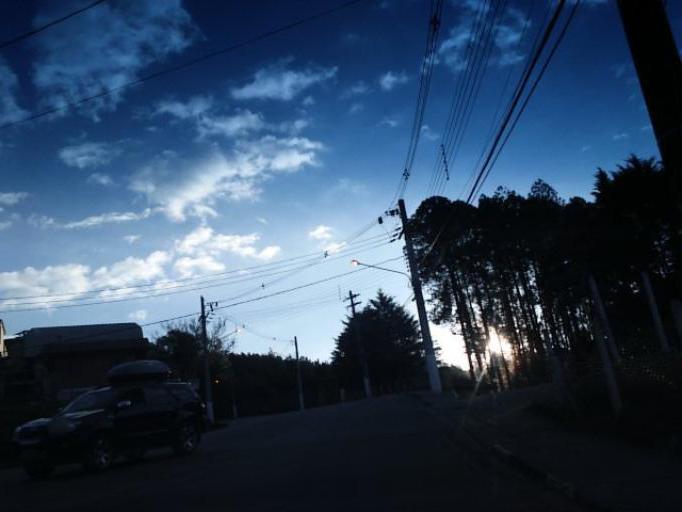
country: BR
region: Sao Paulo
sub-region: Campos Do Jordao
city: Campos do Jordao
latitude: -22.7376
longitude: -45.5971
